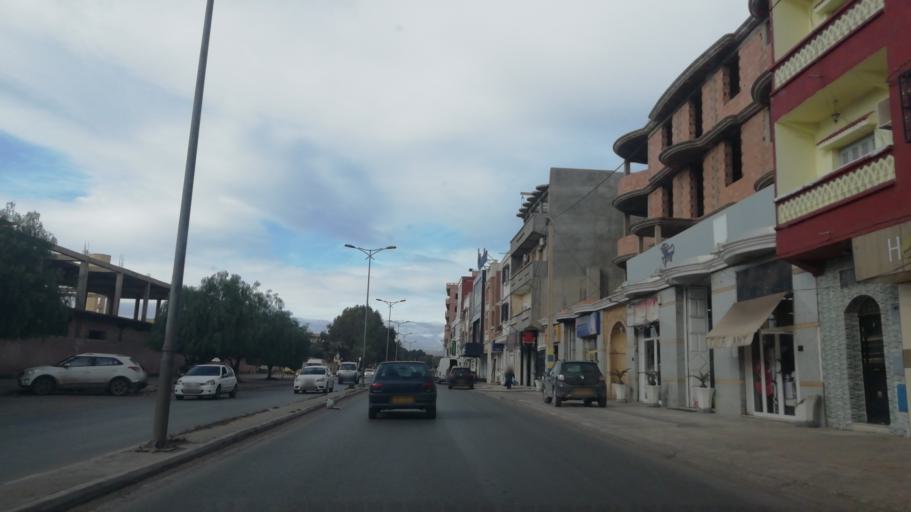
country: DZ
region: Oran
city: Bir el Djir
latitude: 35.7129
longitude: -0.5862
